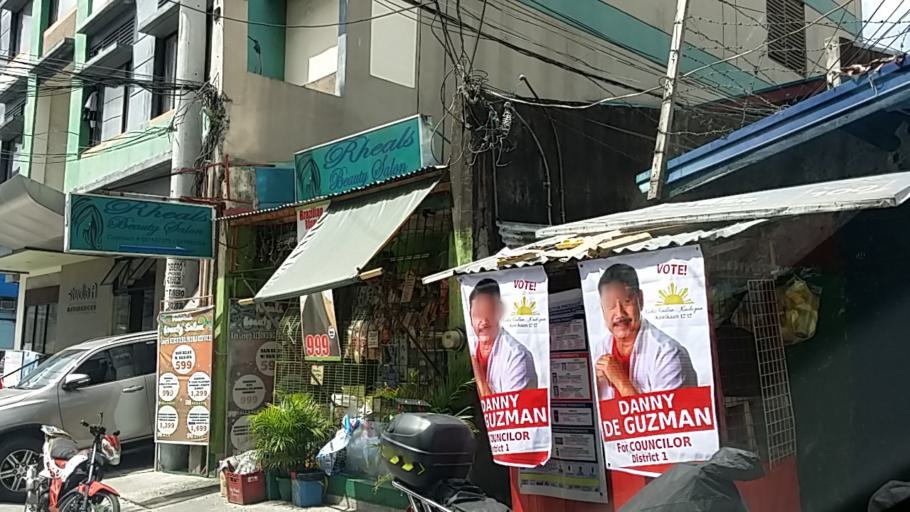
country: PH
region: Metro Manila
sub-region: Mandaluyong
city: Mandaluyong City
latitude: 14.5810
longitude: 121.0513
